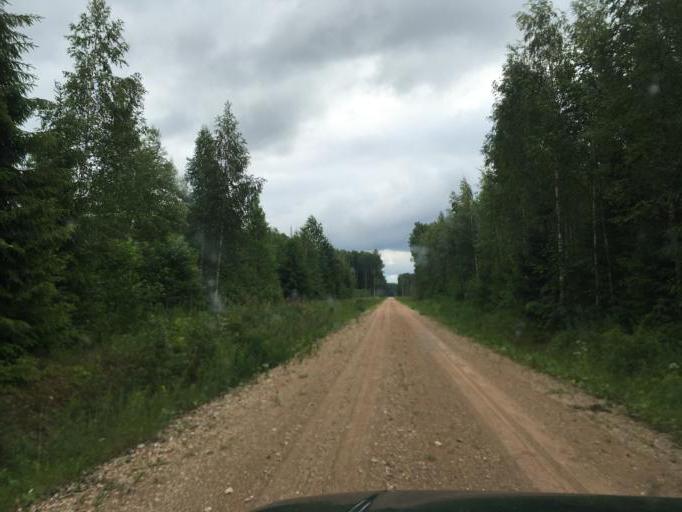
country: LV
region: Vilaka
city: Vilaka
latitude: 57.3871
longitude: 27.5008
